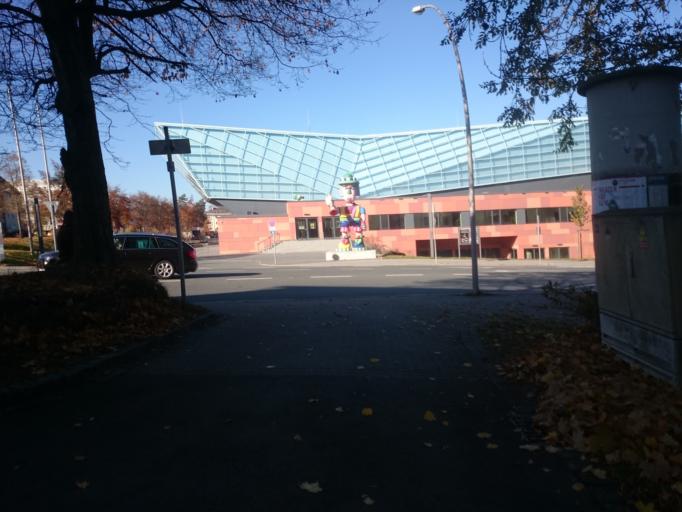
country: DE
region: Bavaria
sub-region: Upper Franconia
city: Hof
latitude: 50.3194
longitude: 11.9038
